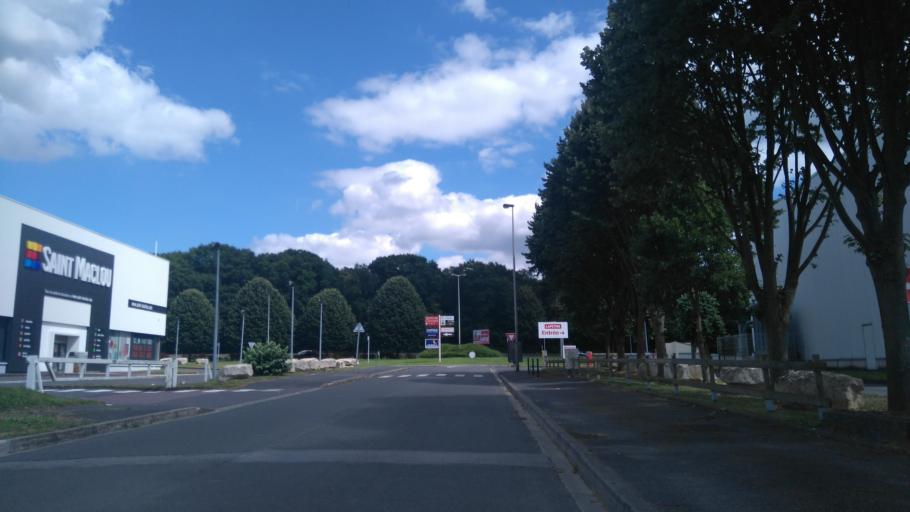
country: FR
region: Picardie
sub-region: Departement de l'Oise
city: Saint-Maximin
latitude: 49.2310
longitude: 2.4684
